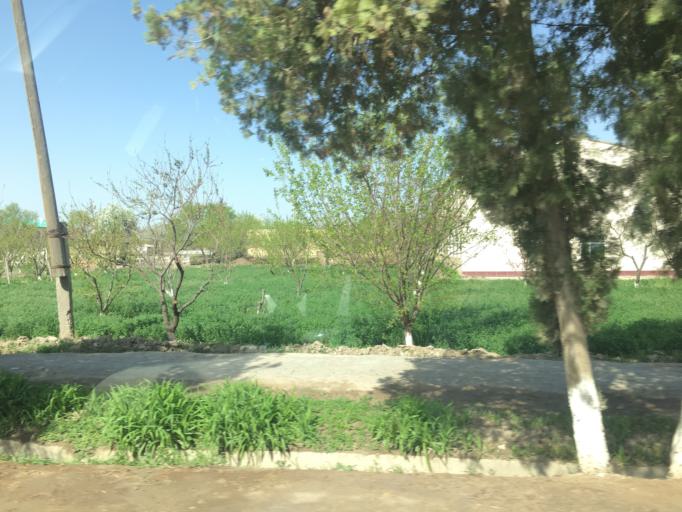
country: TM
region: Lebap
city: Turkmenabat
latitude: 38.9647
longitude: 63.6522
